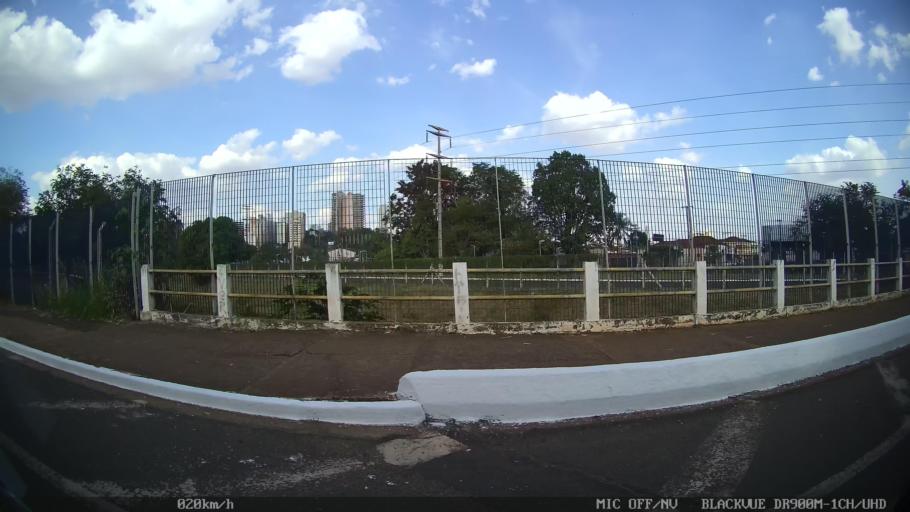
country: BR
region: Sao Paulo
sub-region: Ribeirao Preto
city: Ribeirao Preto
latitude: -21.1769
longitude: -47.8206
